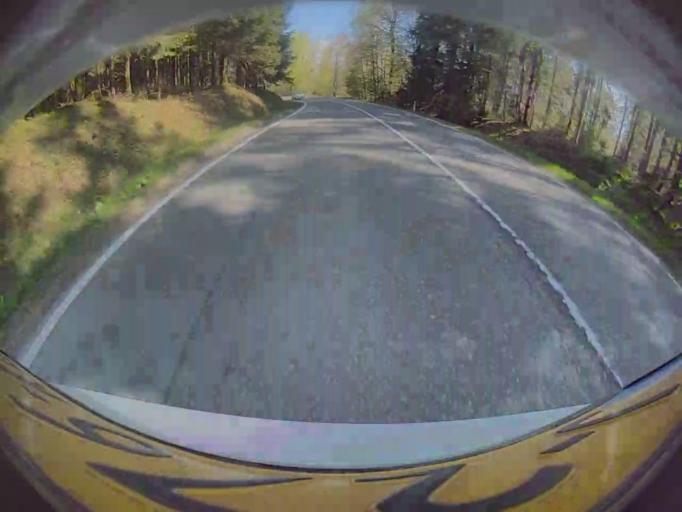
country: BE
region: Wallonia
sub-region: Province du Luxembourg
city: Tellin
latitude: 50.0185
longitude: 5.2055
